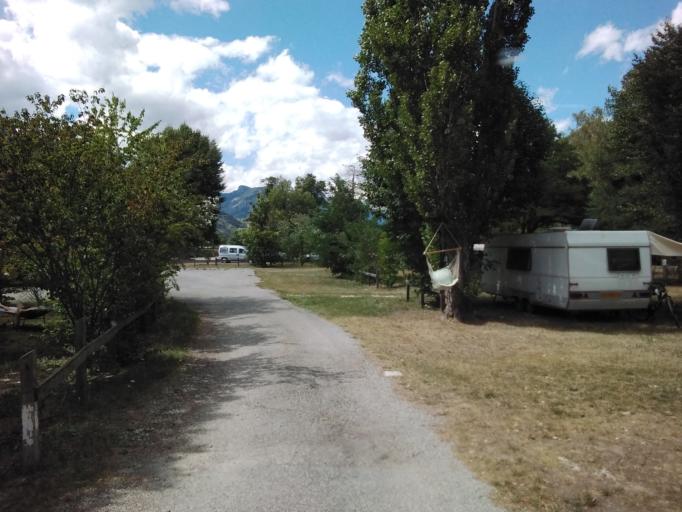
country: FR
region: Provence-Alpes-Cote d'Azur
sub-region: Departement des Hautes-Alpes
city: Guillestre
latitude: 44.7048
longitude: 6.6030
